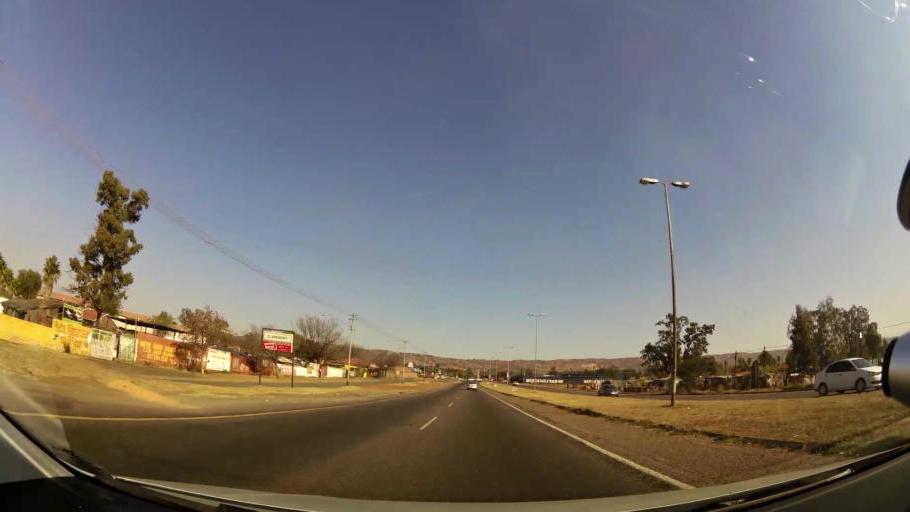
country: ZA
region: Gauteng
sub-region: City of Tshwane Metropolitan Municipality
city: Pretoria
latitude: -25.7073
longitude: 28.1375
